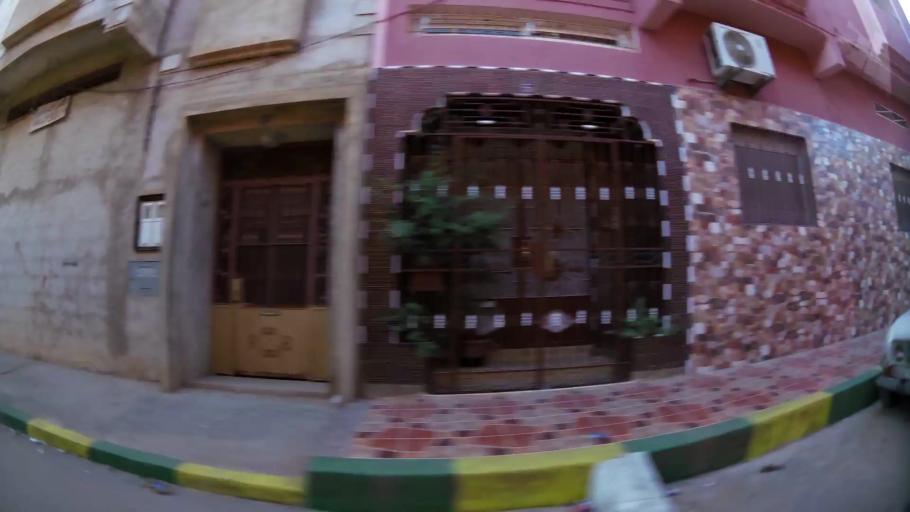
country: MA
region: Oriental
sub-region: Berkane-Taourirt
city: Berkane
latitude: 34.9244
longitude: -2.3161
